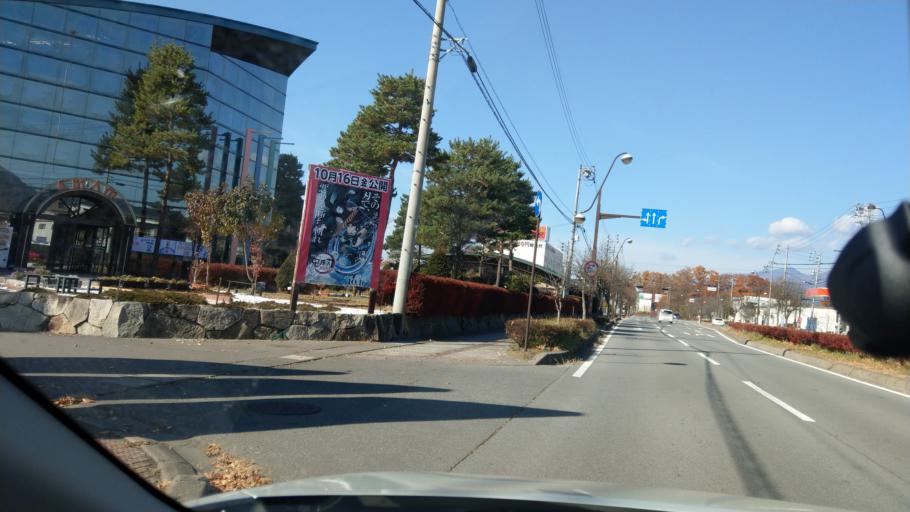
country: JP
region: Nagano
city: Komoro
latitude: 36.2866
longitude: 138.4790
